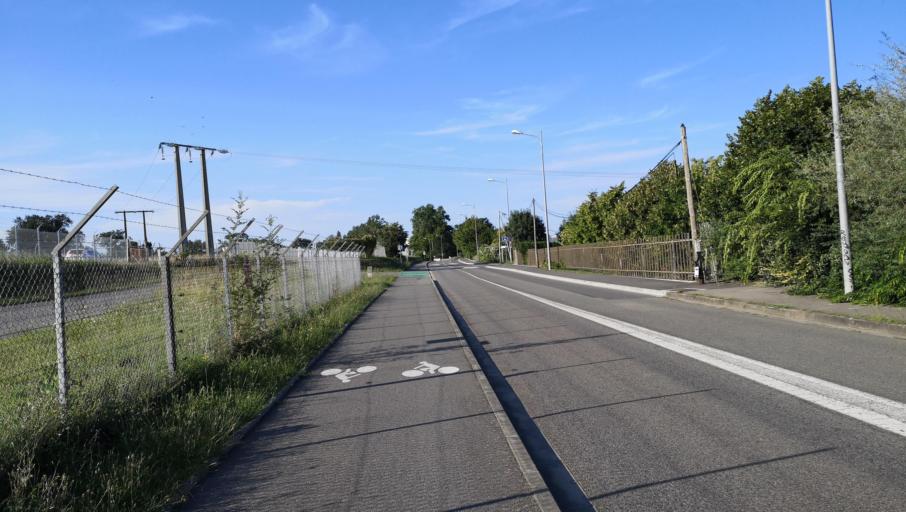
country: FR
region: Midi-Pyrenees
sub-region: Departement de la Haute-Garonne
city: Blagnac
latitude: 43.6167
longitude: 1.3879
